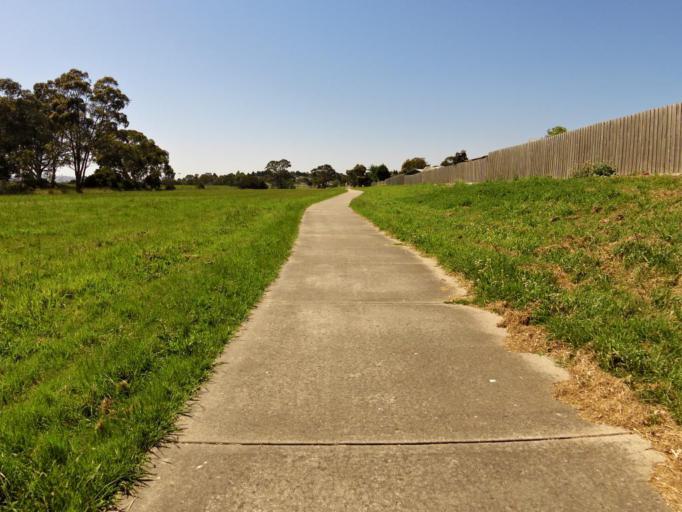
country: AU
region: Victoria
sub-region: Casey
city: Hallam
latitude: -38.0204
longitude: 145.2542
